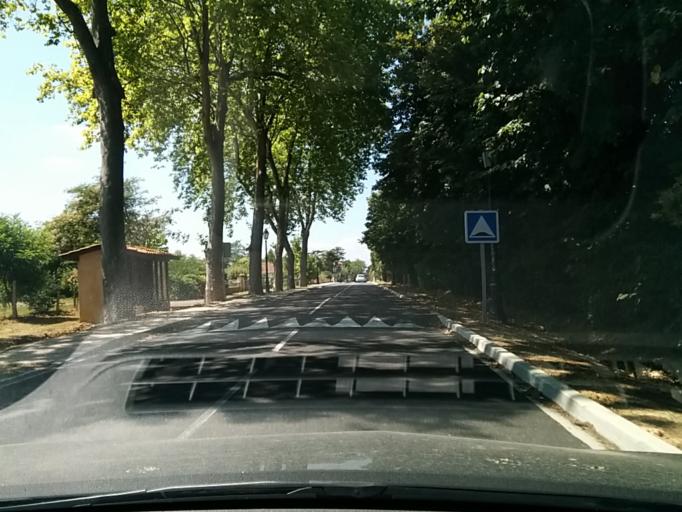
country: FR
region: Midi-Pyrenees
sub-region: Departement du Gers
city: Le Houga
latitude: 43.7679
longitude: -0.1211
